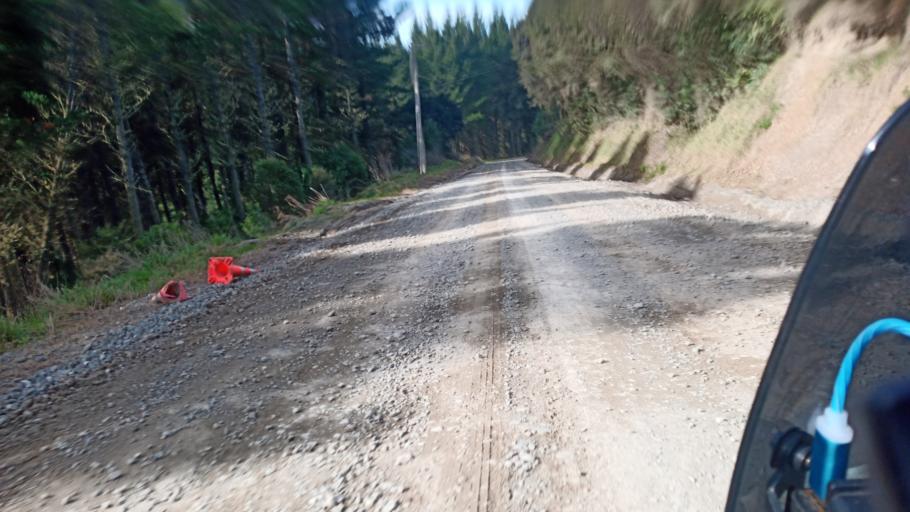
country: NZ
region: Gisborne
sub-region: Gisborne District
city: Gisborne
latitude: -38.1207
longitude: 178.1486
